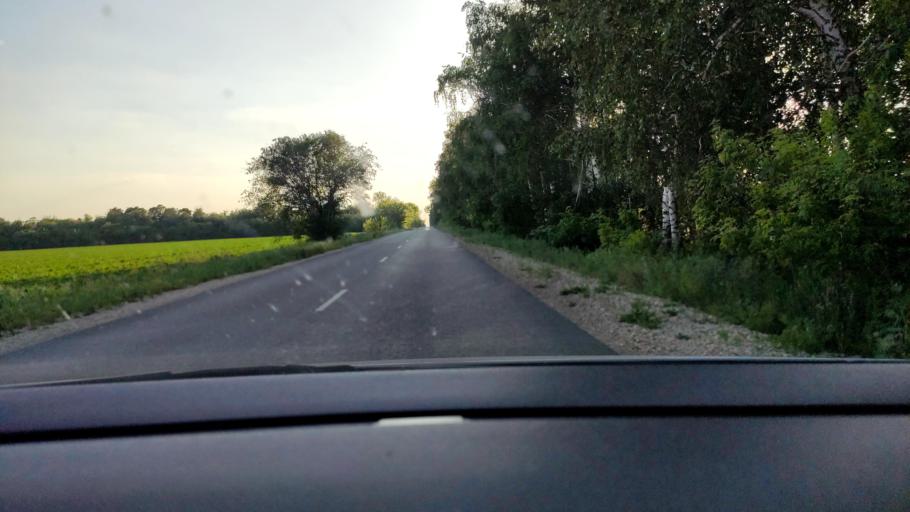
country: RU
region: Voronezj
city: Podkletnoye
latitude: 51.5065
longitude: 39.3761
